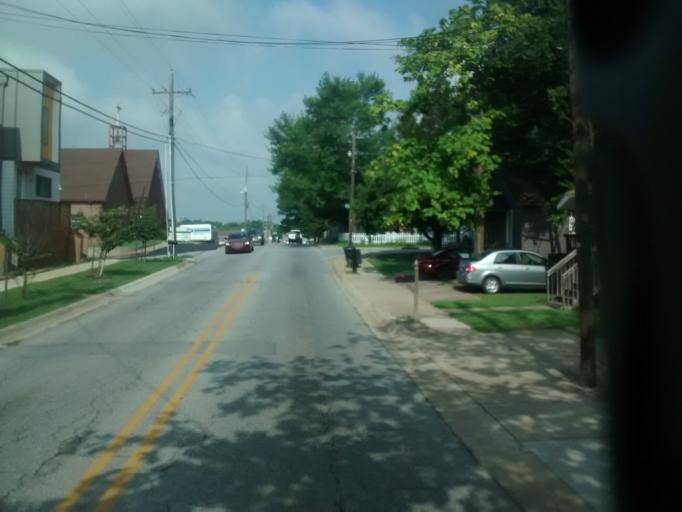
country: US
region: Arkansas
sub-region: Washington County
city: Fayetteville
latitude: 36.0564
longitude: -94.1615
